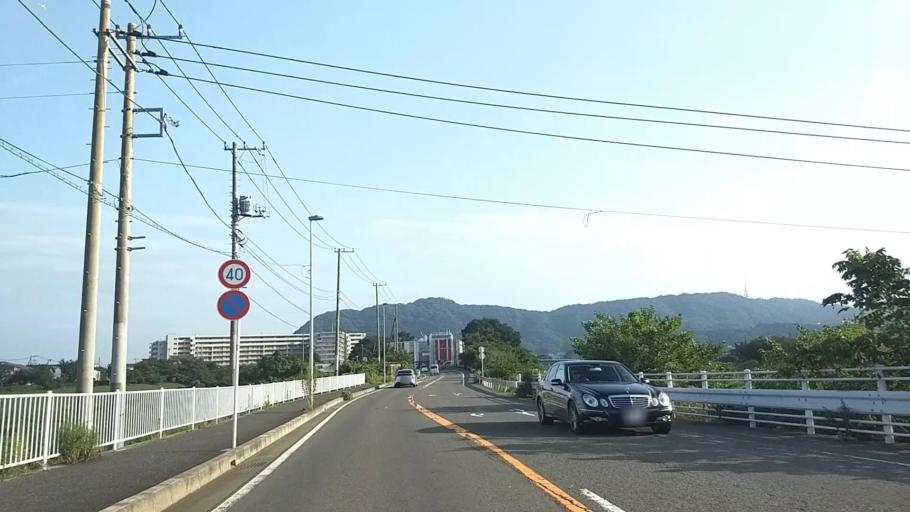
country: JP
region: Kanagawa
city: Hiratsuka
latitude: 35.3395
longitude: 139.3222
